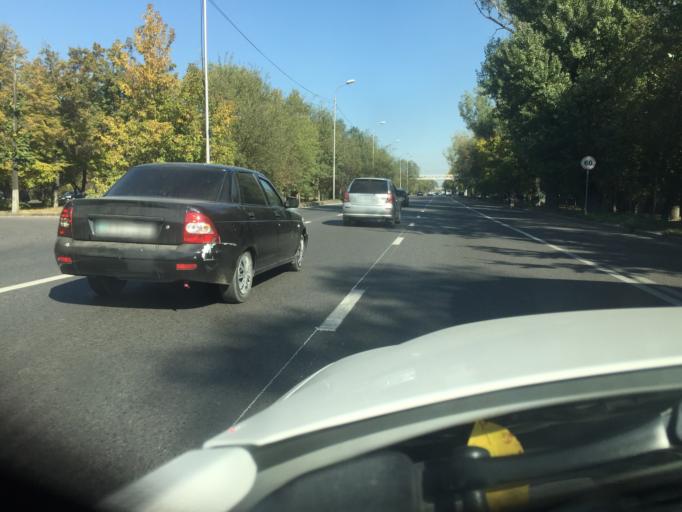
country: KZ
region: Almaty Qalasy
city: Almaty
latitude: 43.2610
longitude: 76.8932
